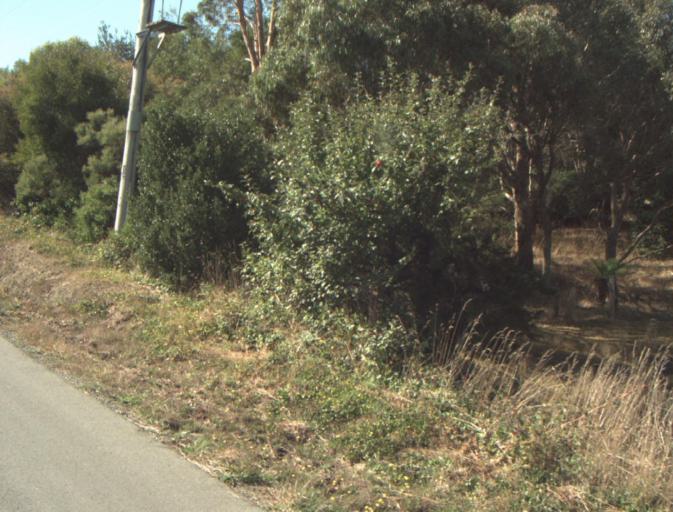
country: AU
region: Tasmania
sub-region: Launceston
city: Mayfield
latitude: -41.2350
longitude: 147.2345
